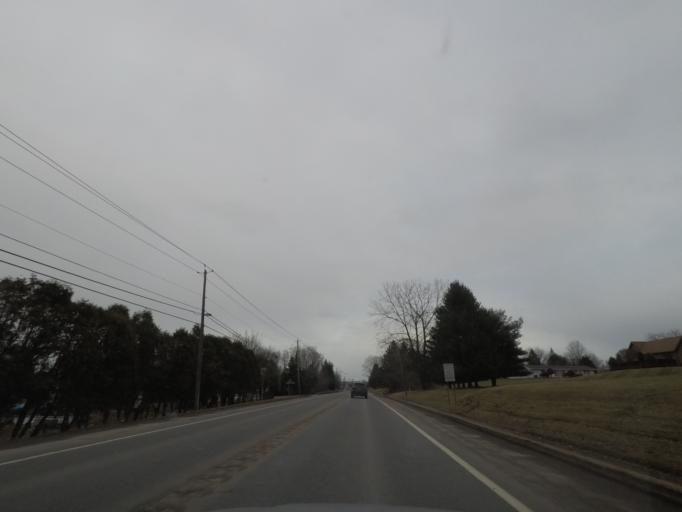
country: US
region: New York
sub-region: Madison County
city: Oneida
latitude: 43.0775
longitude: -75.6699
